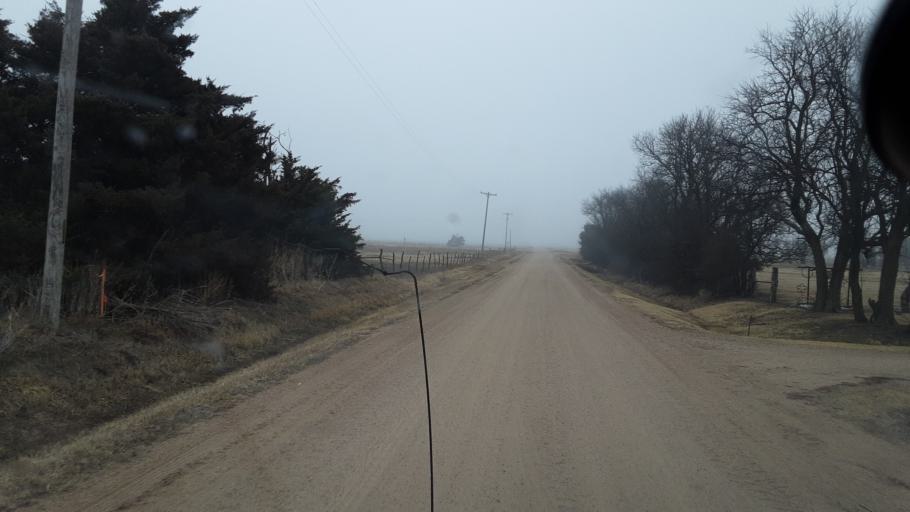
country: US
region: Kansas
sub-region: Reno County
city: South Hutchinson
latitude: 37.9863
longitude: -97.9957
